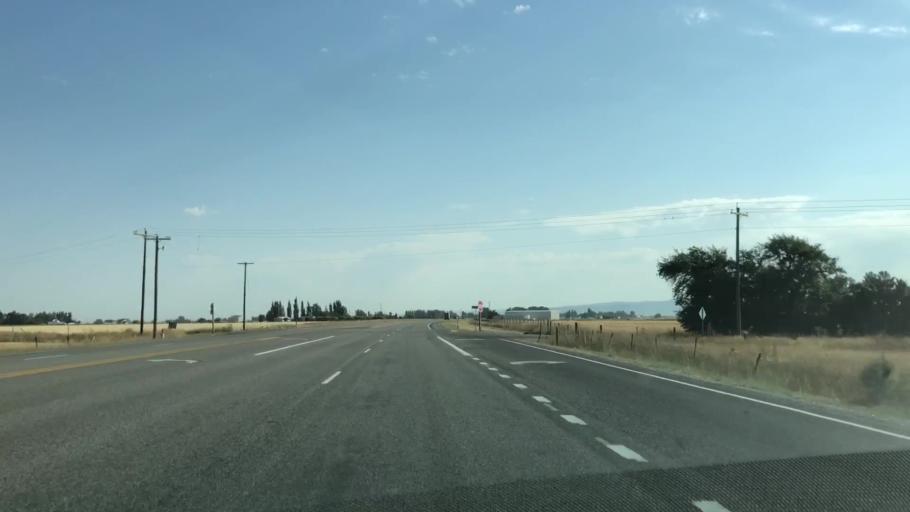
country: US
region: Idaho
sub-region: Bonneville County
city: Iona
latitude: 43.5888
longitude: -111.8849
